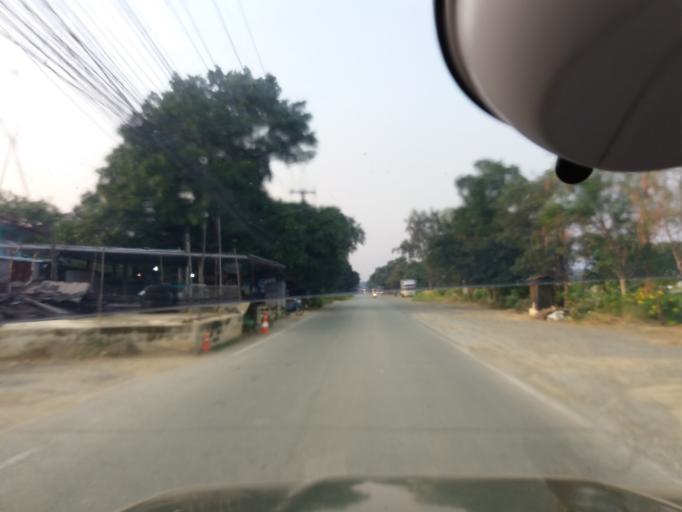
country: TH
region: Sing Buri
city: Sing Buri
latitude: 14.8871
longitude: 100.3996
